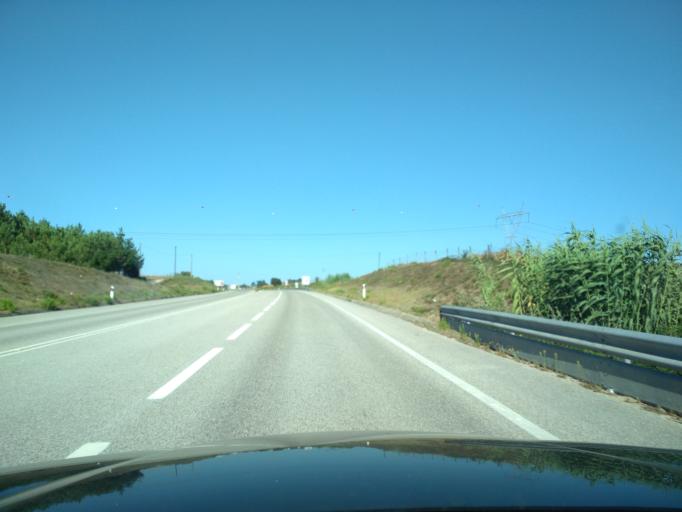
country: PT
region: Leiria
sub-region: Pombal
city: Lourical
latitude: 39.9888
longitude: -8.7784
